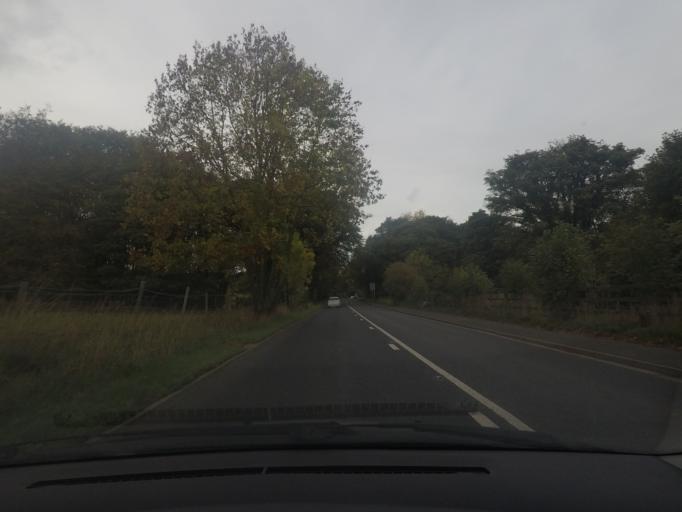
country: GB
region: England
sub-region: Sheffield
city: Chapletown
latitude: 53.4587
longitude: -1.4990
